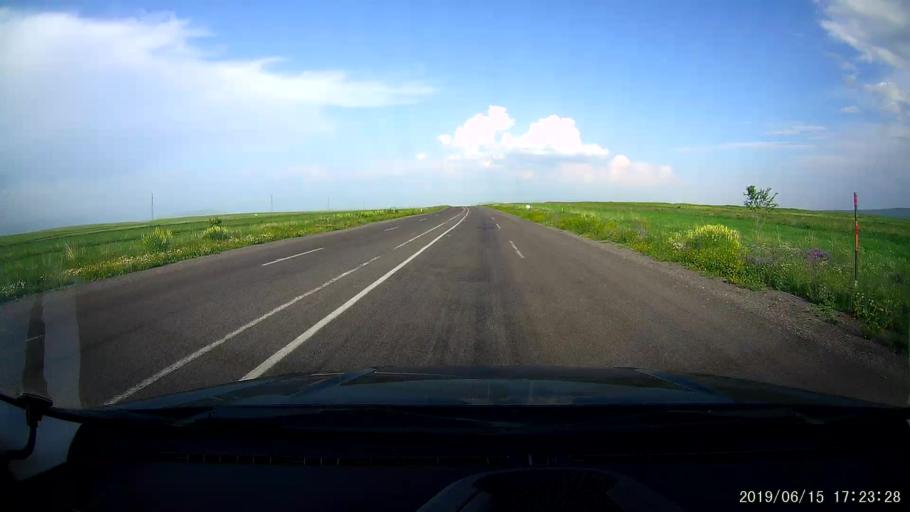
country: TR
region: Kars
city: Basgedikler
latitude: 40.6167
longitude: 43.3635
